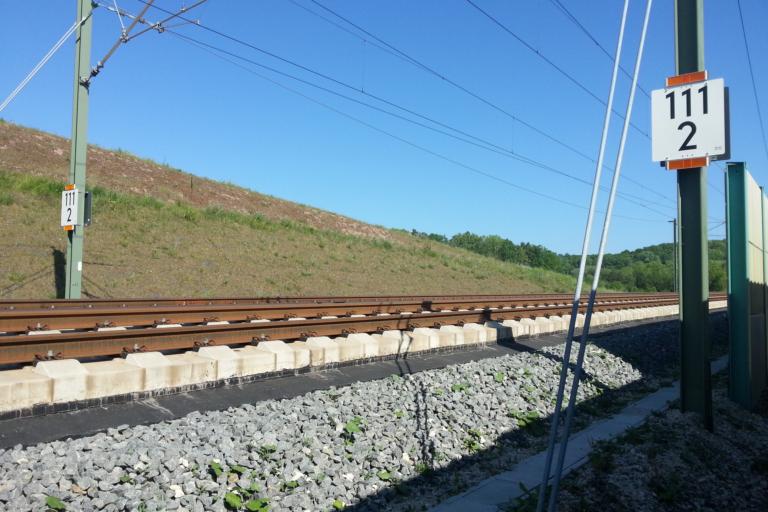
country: DE
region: Bavaria
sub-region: Upper Franconia
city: Rodental
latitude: 50.3084
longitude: 11.0067
